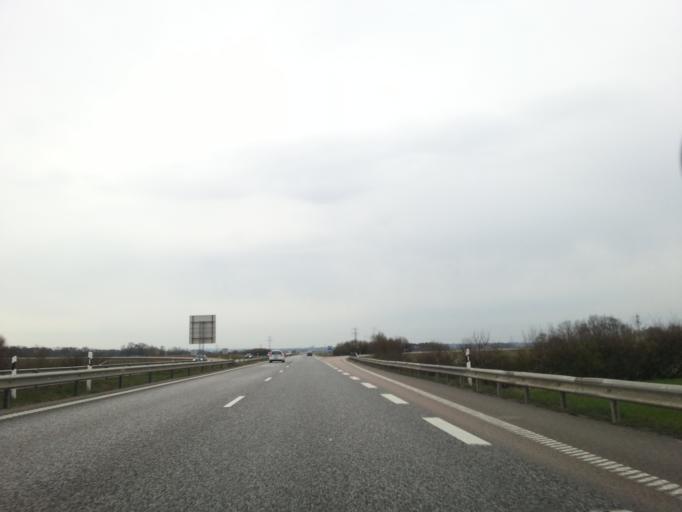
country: SE
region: Skane
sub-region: Angelholms Kommun
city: Munka-Ljungby
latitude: 56.3169
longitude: 12.9127
